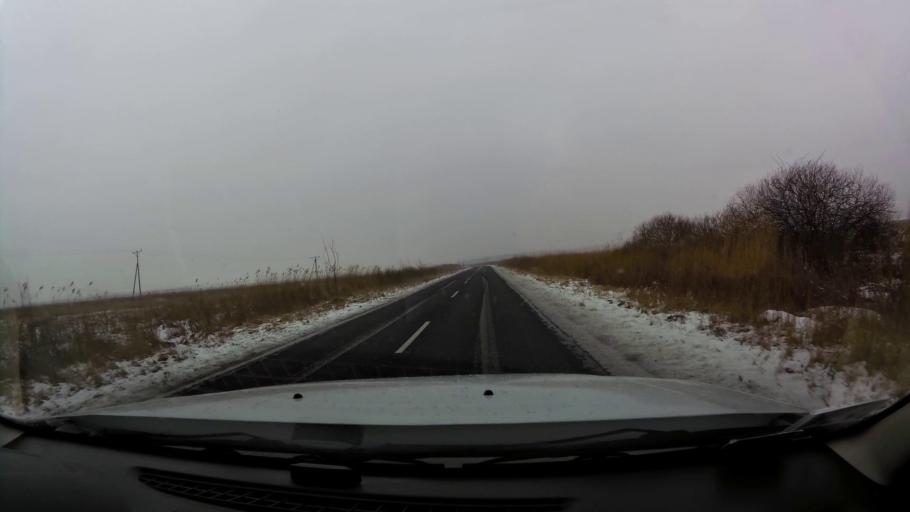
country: PL
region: West Pomeranian Voivodeship
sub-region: Powiat gryficki
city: Mrzezyno
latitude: 54.1249
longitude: 15.2720
